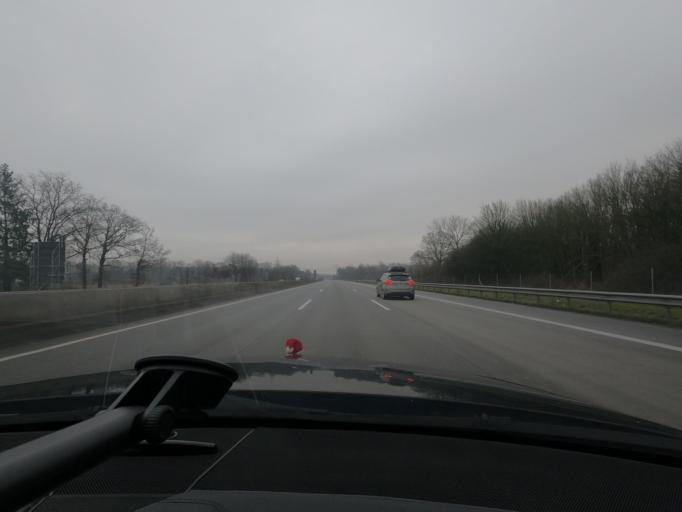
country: DE
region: Schleswig-Holstein
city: Quickborn
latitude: 53.7086
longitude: 9.9402
